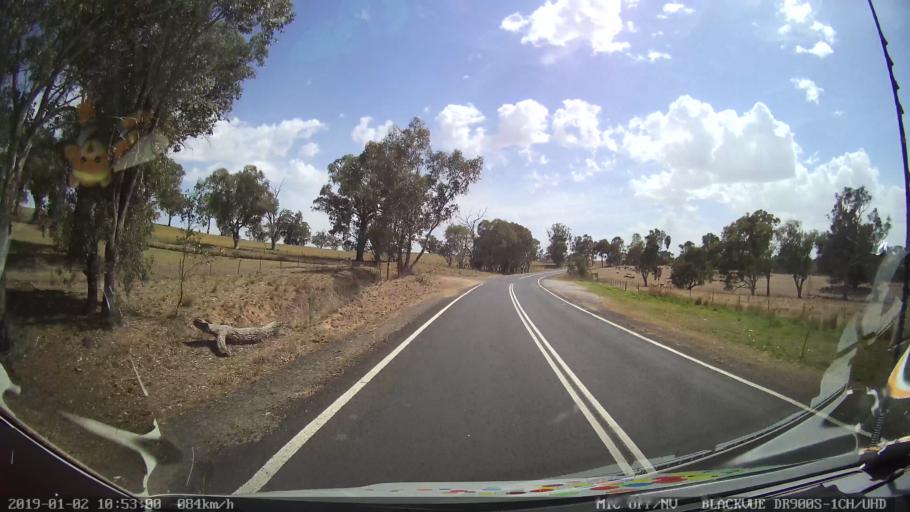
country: AU
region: New South Wales
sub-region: Cootamundra
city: Cootamundra
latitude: -34.6822
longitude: 148.2716
